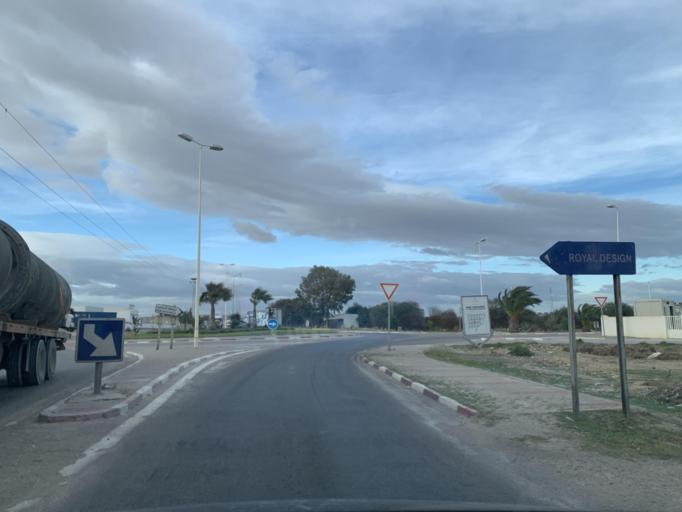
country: TN
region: Susah
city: Harqalah
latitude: 36.1102
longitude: 10.3861
